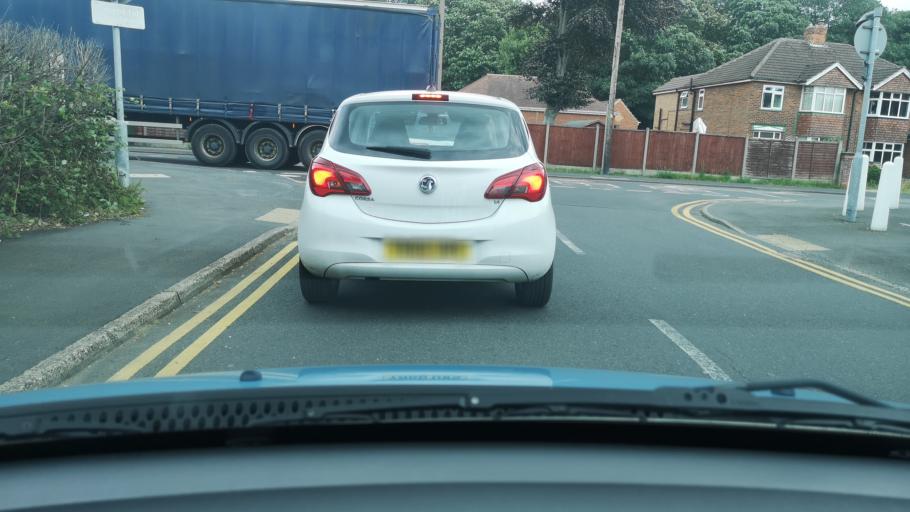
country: GB
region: England
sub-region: North Lincolnshire
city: Scunthorpe
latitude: 53.5889
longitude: -0.6842
